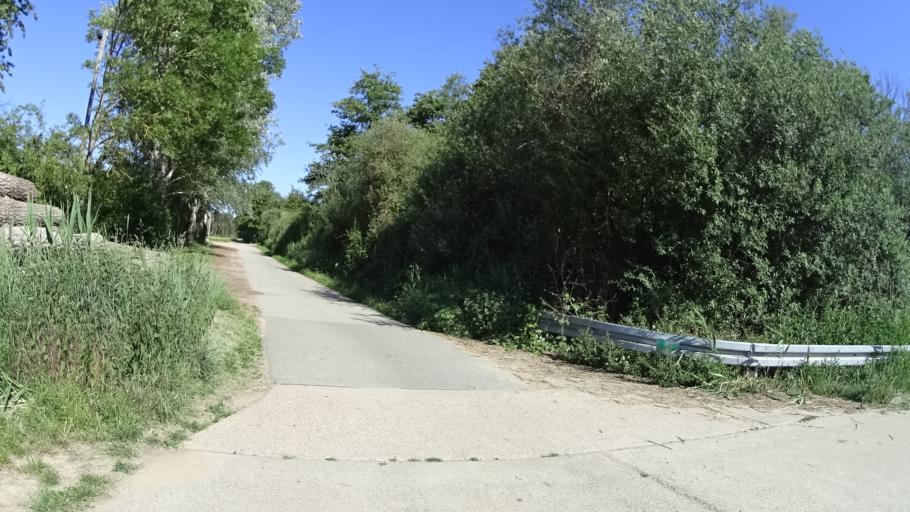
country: DE
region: Hesse
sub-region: Regierungsbezirk Darmstadt
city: Alsbach-Hahnlein
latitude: 49.7457
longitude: 8.5844
